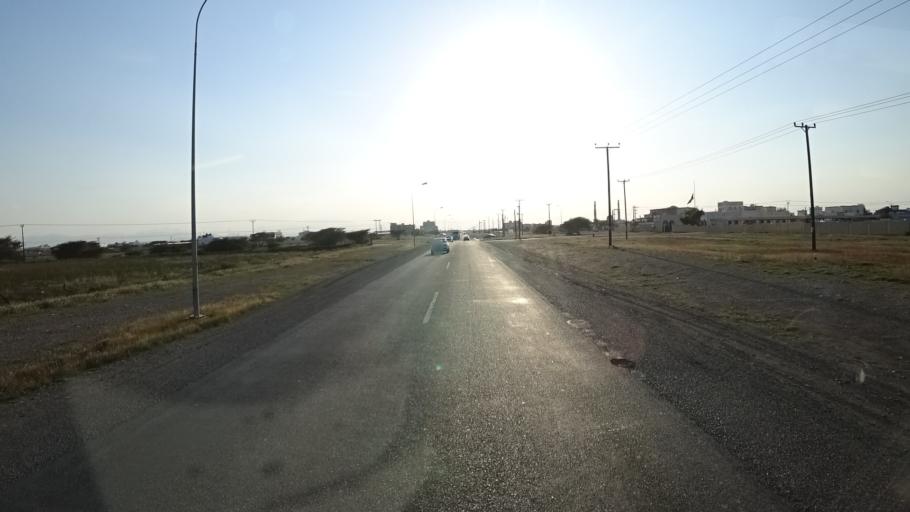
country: OM
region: Al Batinah
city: Al Khaburah
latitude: 23.9553
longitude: 57.0652
